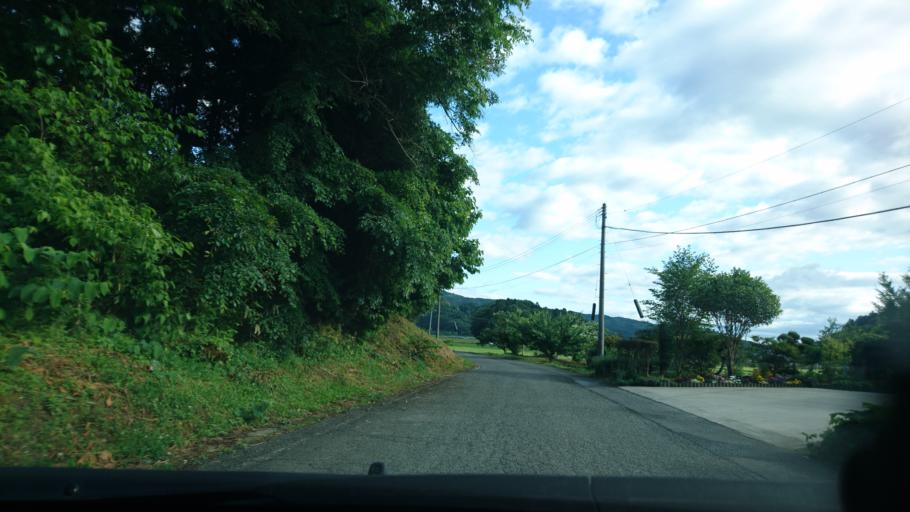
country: JP
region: Iwate
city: Ichinoseki
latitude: 38.8592
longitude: 141.2847
